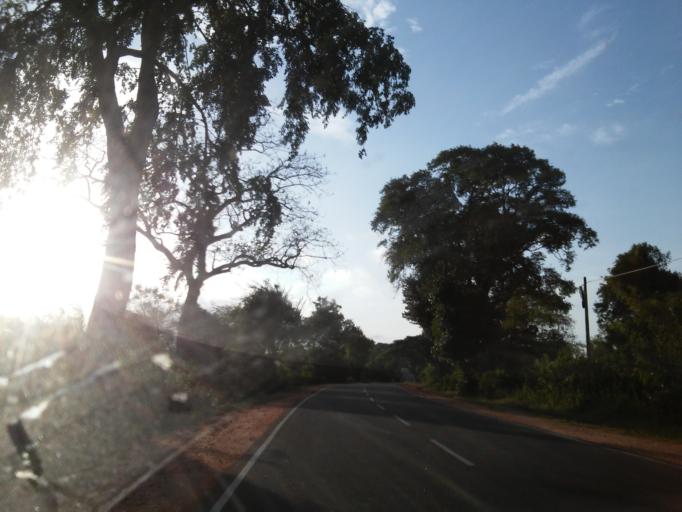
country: LK
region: Central
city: Sigiriya
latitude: 8.0961
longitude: 80.6062
